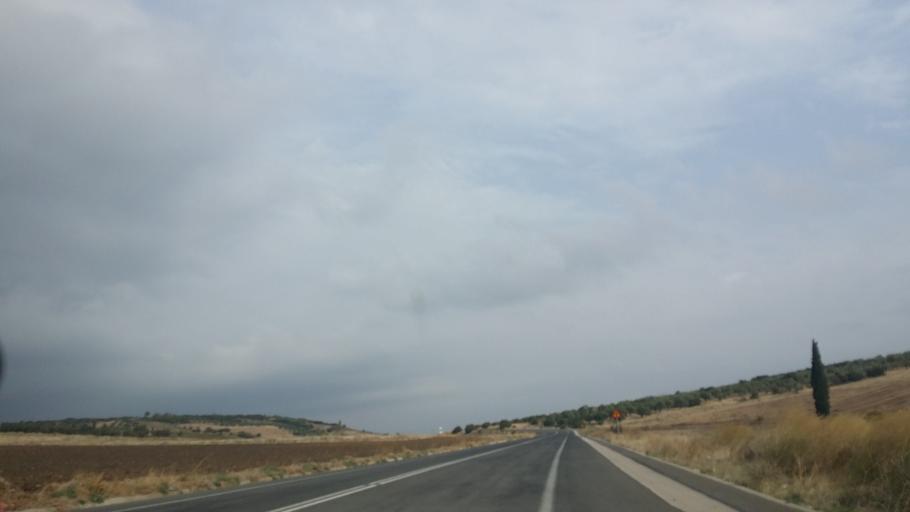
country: GR
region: Central Greece
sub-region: Nomos Voiotias
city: Thespies
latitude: 38.2768
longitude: 23.1041
